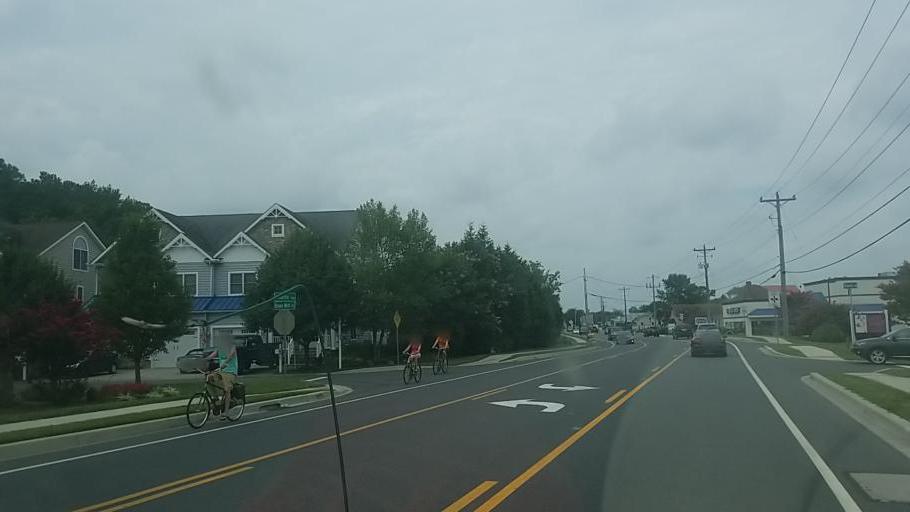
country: US
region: Delaware
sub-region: Sussex County
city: Ocean View
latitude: 38.5430
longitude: -75.0824
